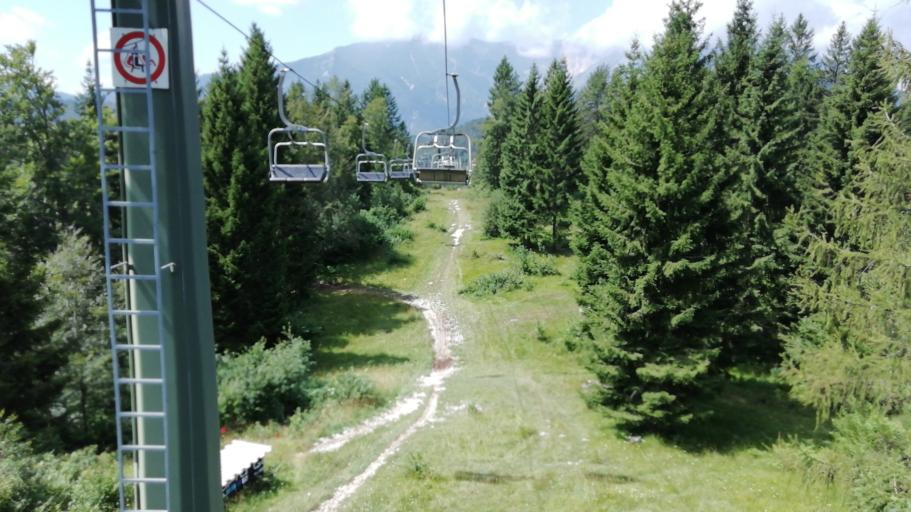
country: IT
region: Trentino-Alto Adige
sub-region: Provincia di Trento
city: Gionghi-Cappella
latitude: 45.9502
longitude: 11.2694
